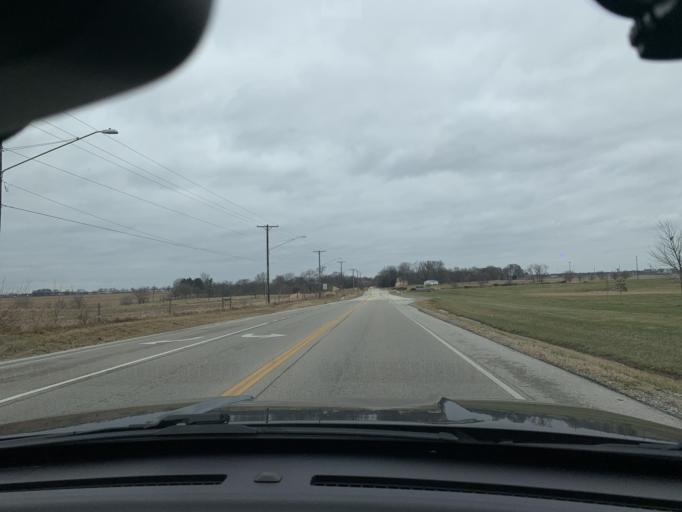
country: US
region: Illinois
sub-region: Sangamon County
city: Chatham
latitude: 39.7208
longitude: -89.6909
